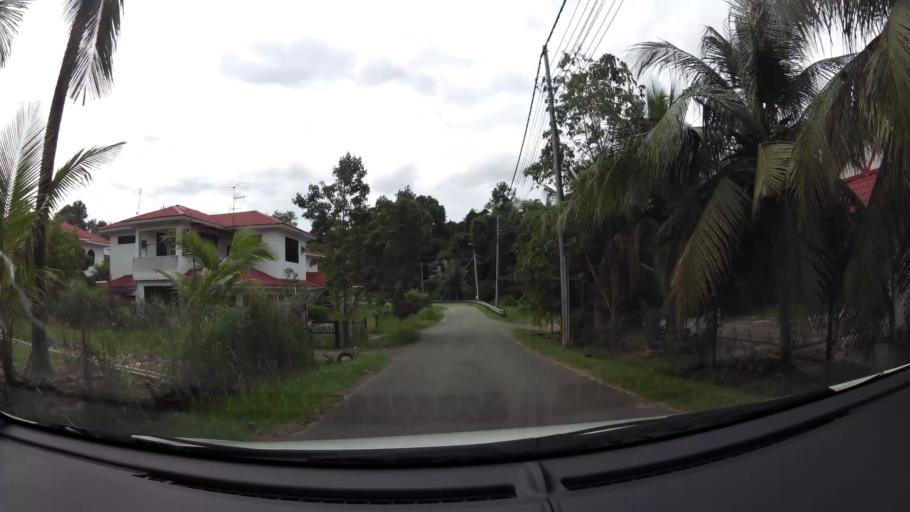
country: BN
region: Brunei and Muara
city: Bandar Seri Begawan
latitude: 4.8871
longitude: 114.8943
